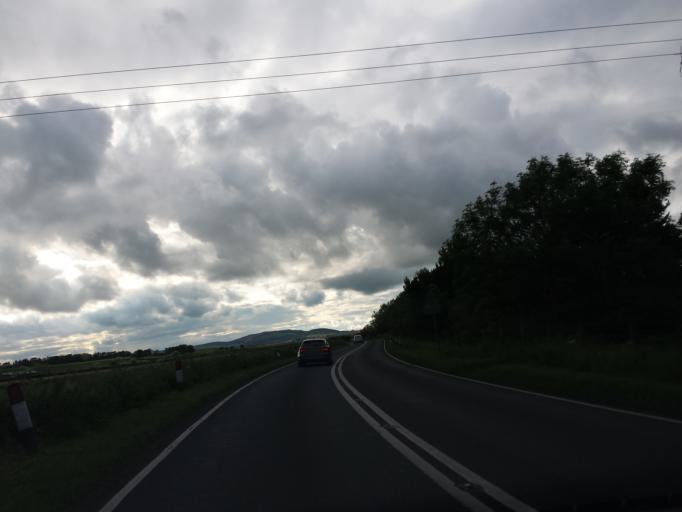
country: GB
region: Scotland
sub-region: Fife
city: Strathkinness
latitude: 56.3503
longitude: -2.8393
